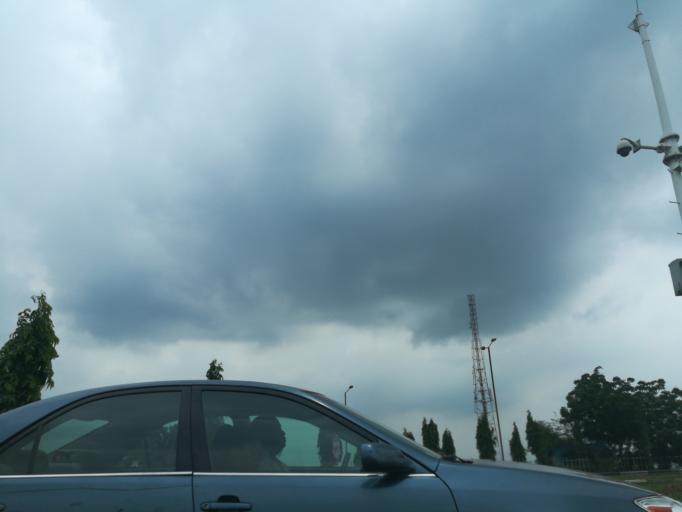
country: NG
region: Lagos
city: Ojota
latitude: 6.5961
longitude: 3.3809
